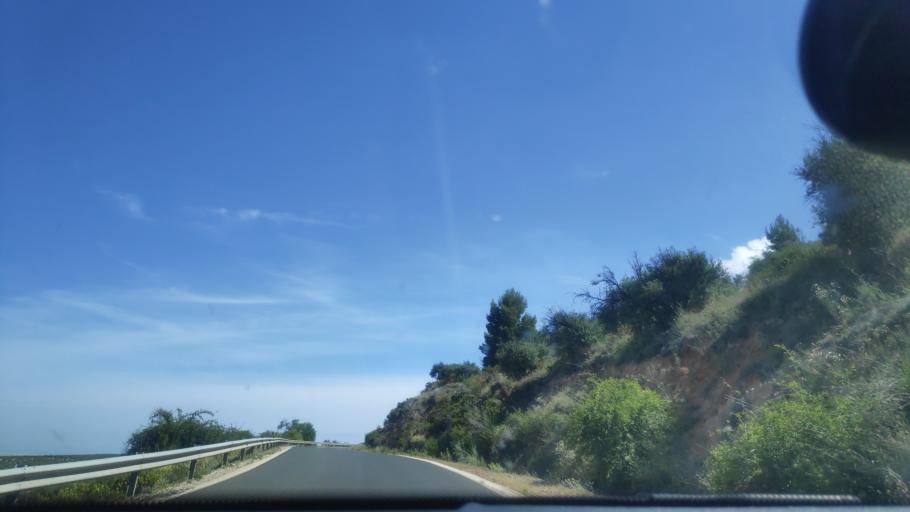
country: ES
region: Andalusia
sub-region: Provincia de Jaen
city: Mancha Real
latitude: 37.7794
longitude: -3.5915
